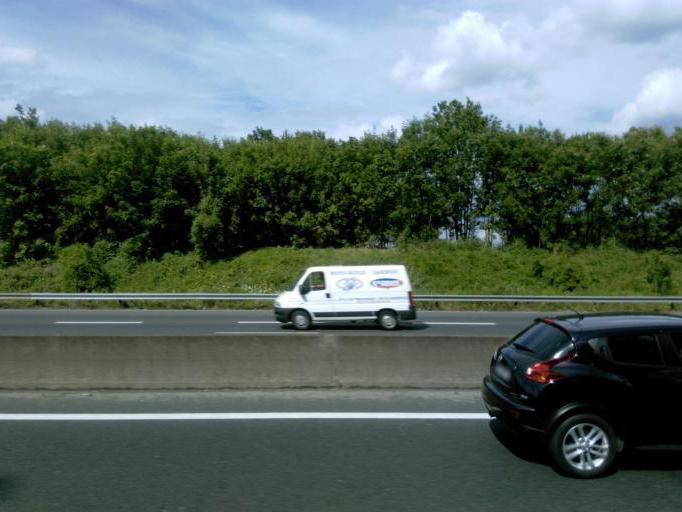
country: FR
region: Ile-de-France
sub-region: Departement du Val-d'Oise
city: Franconville
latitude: 48.9824
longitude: 2.2206
